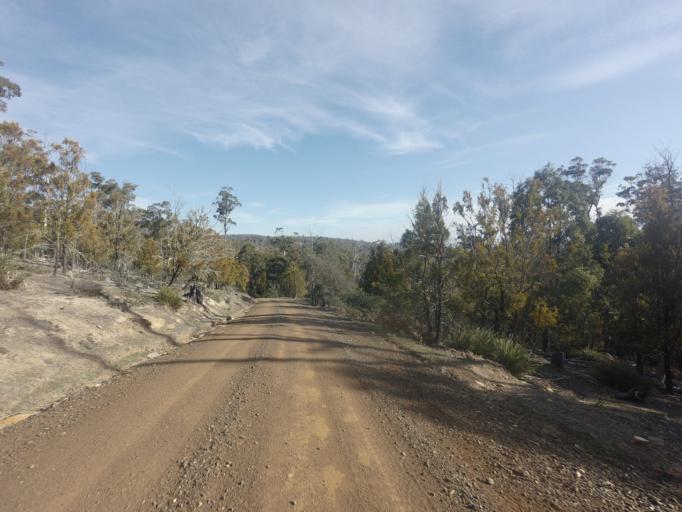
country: AU
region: Tasmania
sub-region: Sorell
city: Sorell
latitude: -42.5296
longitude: 147.4537
